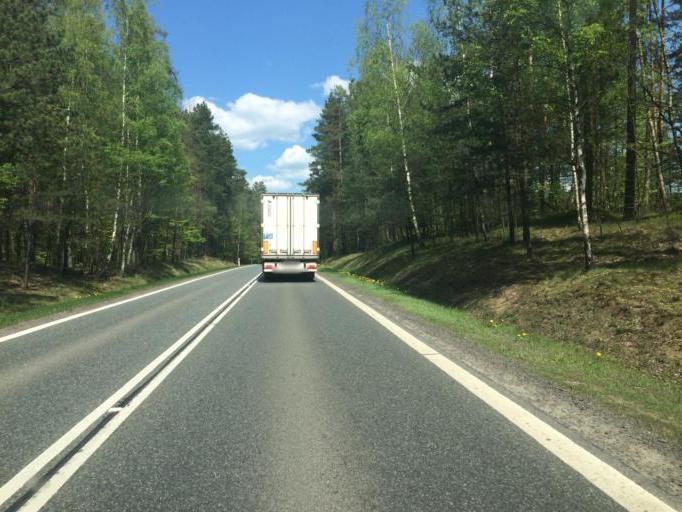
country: PL
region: Warmian-Masurian Voivodeship
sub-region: Powiat ostrodzki
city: Ostroda
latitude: 53.6922
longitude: 20.0866
